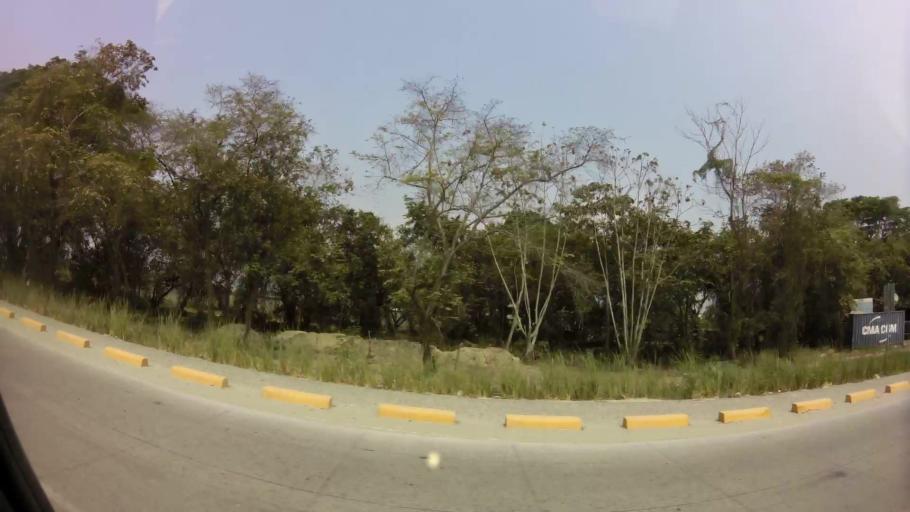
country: HN
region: Cortes
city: San Pedro Sula
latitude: 15.5501
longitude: -87.9977
